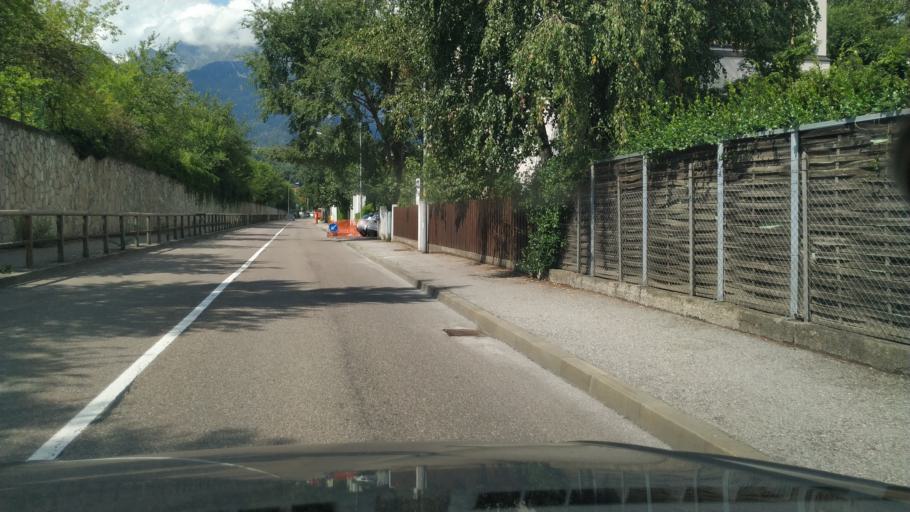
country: IT
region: Trentino-Alto Adige
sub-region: Bolzano
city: Marlengo
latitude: 46.6538
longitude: 11.1521
